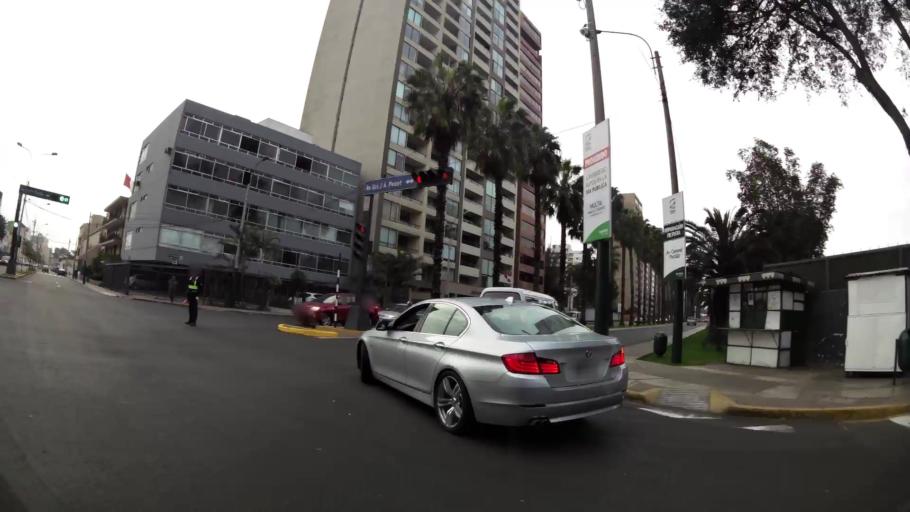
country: PE
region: Lima
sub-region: Lima
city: San Isidro
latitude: -12.1029
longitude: -77.0514
